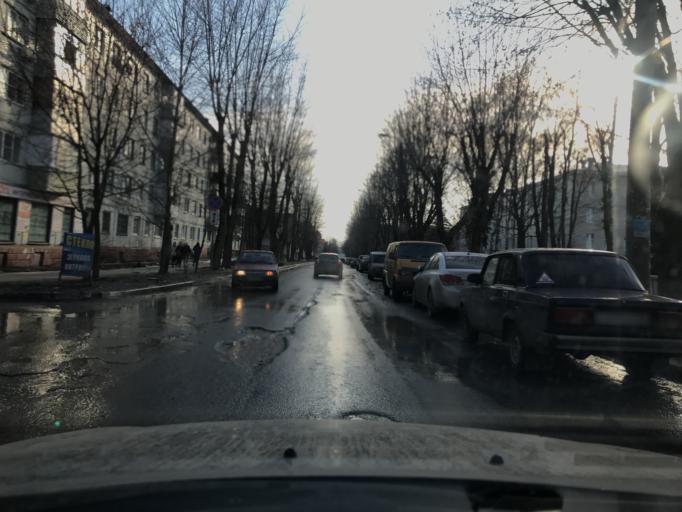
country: RU
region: Kaluga
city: Kaluga
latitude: 54.5178
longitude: 36.2397
